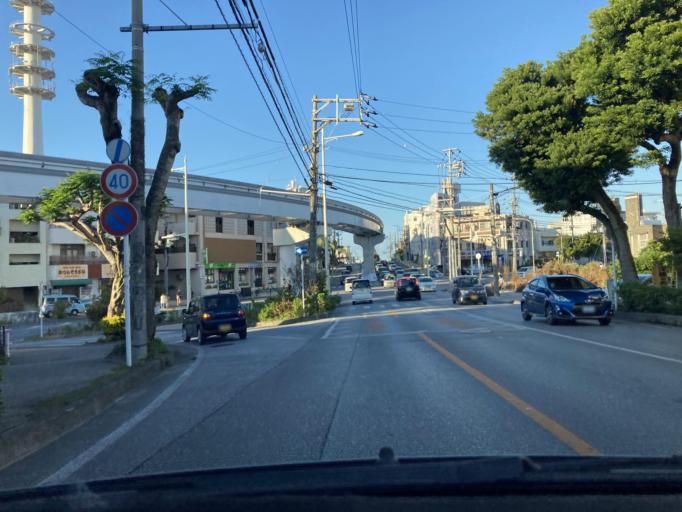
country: JP
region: Okinawa
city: Naha-shi
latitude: 26.2191
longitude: 127.7263
